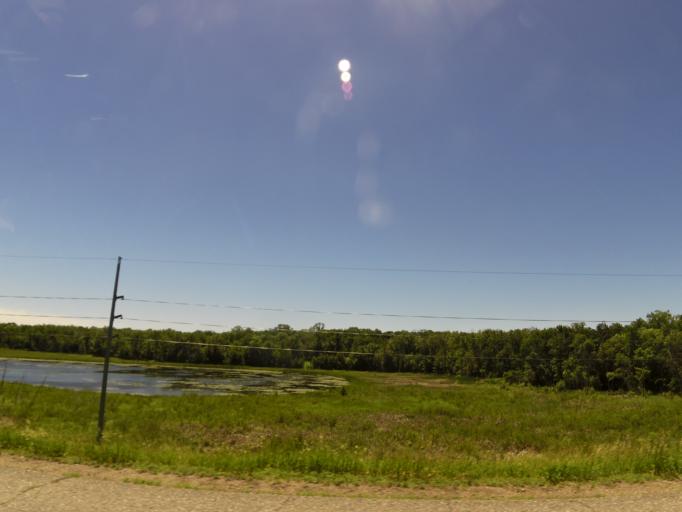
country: US
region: Minnesota
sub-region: Becker County
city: Frazee
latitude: 46.7366
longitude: -95.7446
